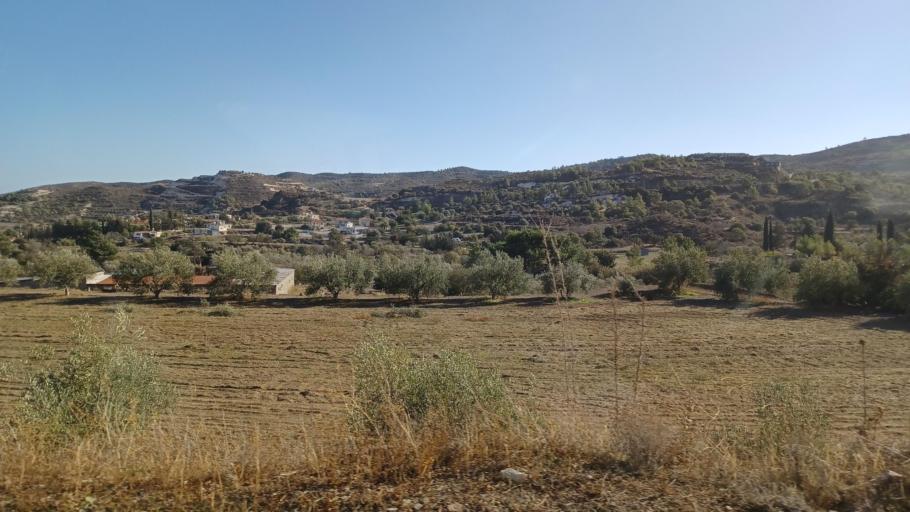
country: CY
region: Limassol
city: Pyrgos
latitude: 34.7803
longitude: 33.2467
